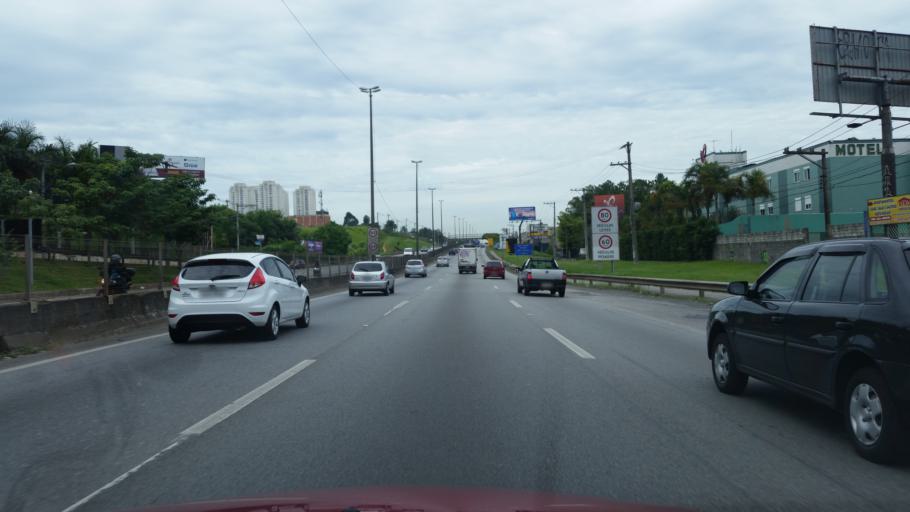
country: BR
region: Sao Paulo
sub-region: Taboao Da Serra
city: Taboao da Serra
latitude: -23.6087
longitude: -46.7694
